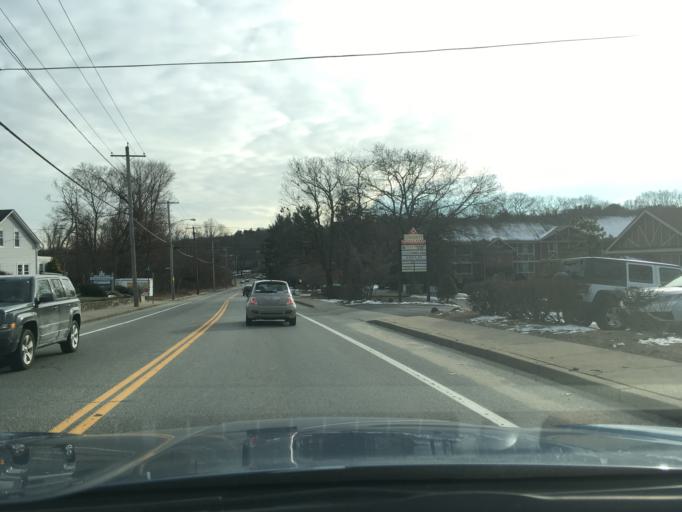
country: US
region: Rhode Island
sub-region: Kent County
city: East Greenwich
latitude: 41.6907
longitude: -71.4563
